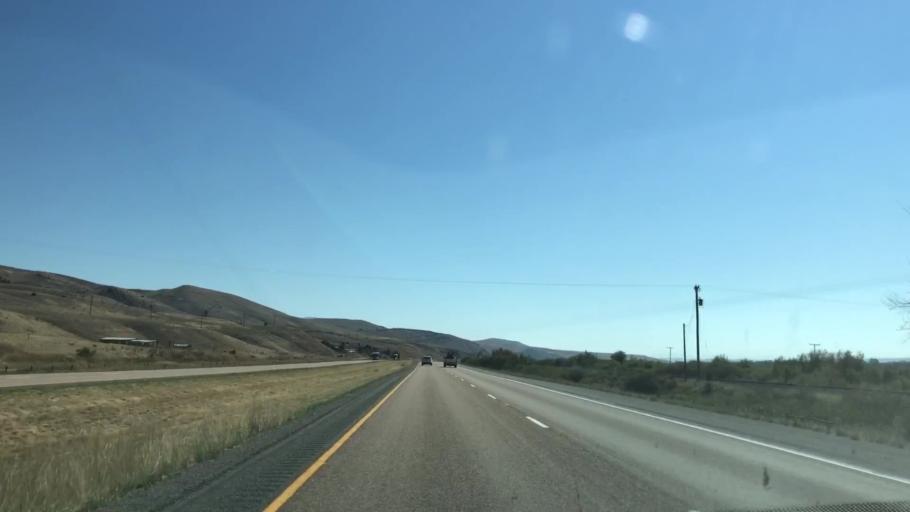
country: US
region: Montana
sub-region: Granite County
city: Philipsburg
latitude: 46.6793
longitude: -113.1837
